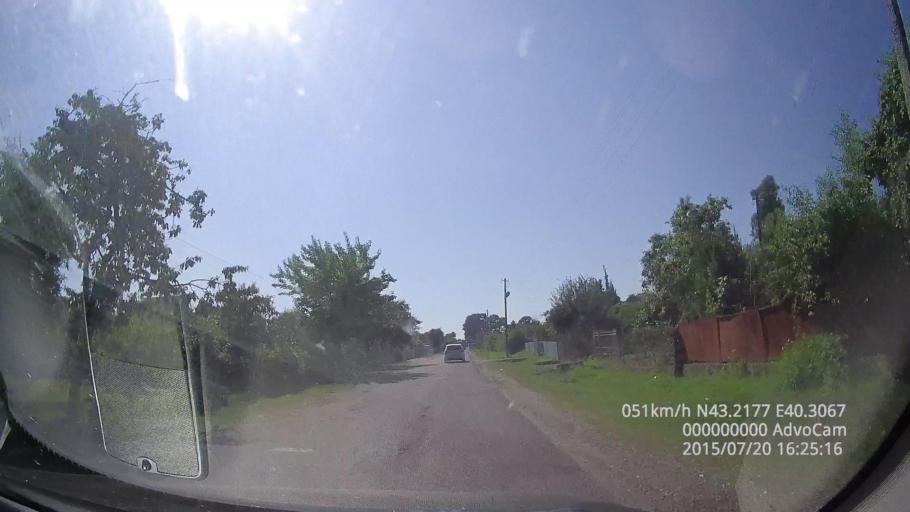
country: GE
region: Abkhazia
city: Bich'vinta
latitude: 43.2177
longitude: 40.3068
